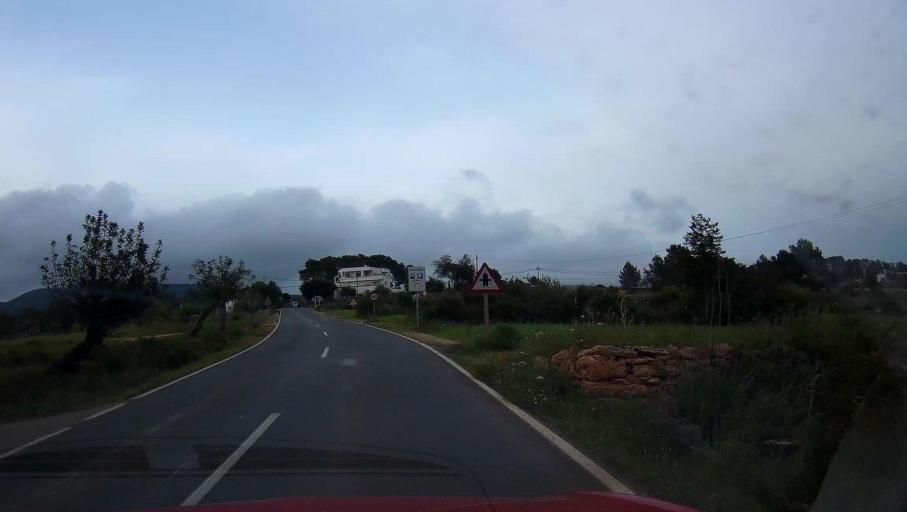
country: ES
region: Balearic Islands
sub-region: Illes Balears
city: Sant Joan de Labritja
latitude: 39.0609
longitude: 1.4700
